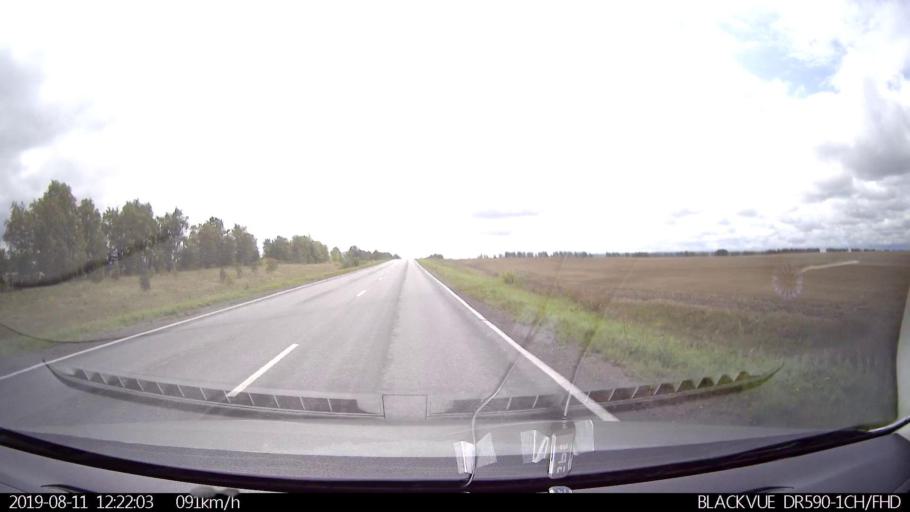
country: RU
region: Ulyanovsk
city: Ignatovka
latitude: 53.9135
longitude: 47.9558
